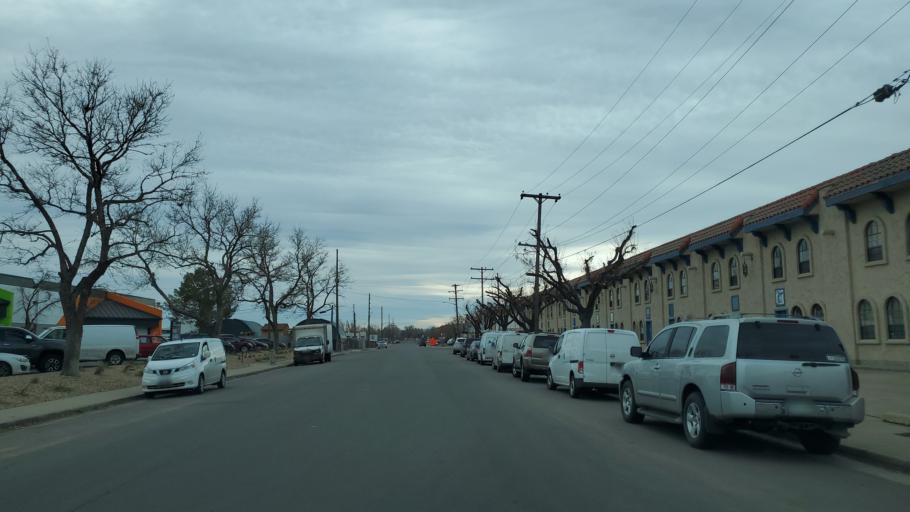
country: US
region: Colorado
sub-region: Denver County
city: Denver
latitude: 39.6959
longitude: -104.9969
